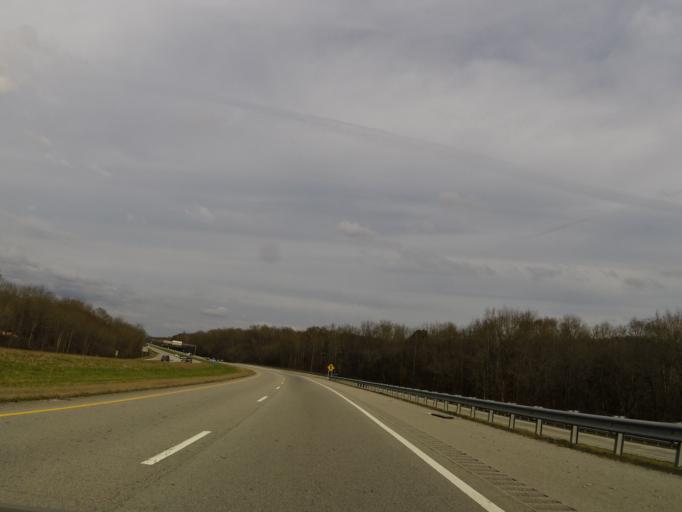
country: US
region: Tennessee
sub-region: Hamilton County
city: Falling Water
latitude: 35.1886
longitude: -85.2450
